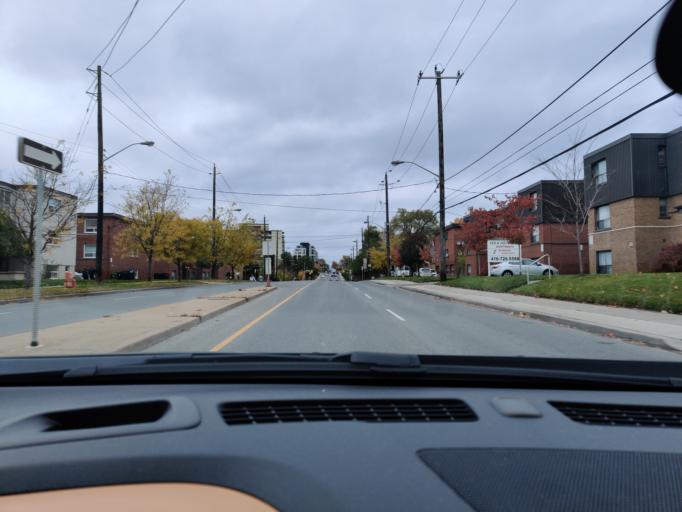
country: CA
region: Ontario
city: Toronto
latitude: 43.7103
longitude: -79.4783
